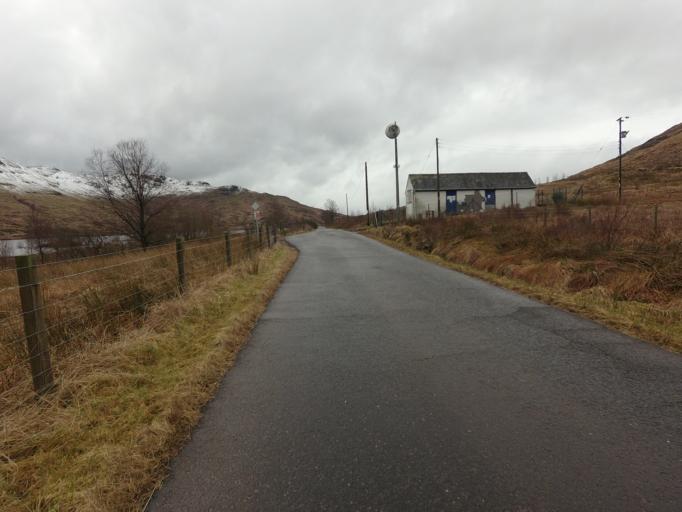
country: GB
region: Scotland
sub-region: West Dunbartonshire
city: Balloch
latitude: 56.2493
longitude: -4.6290
